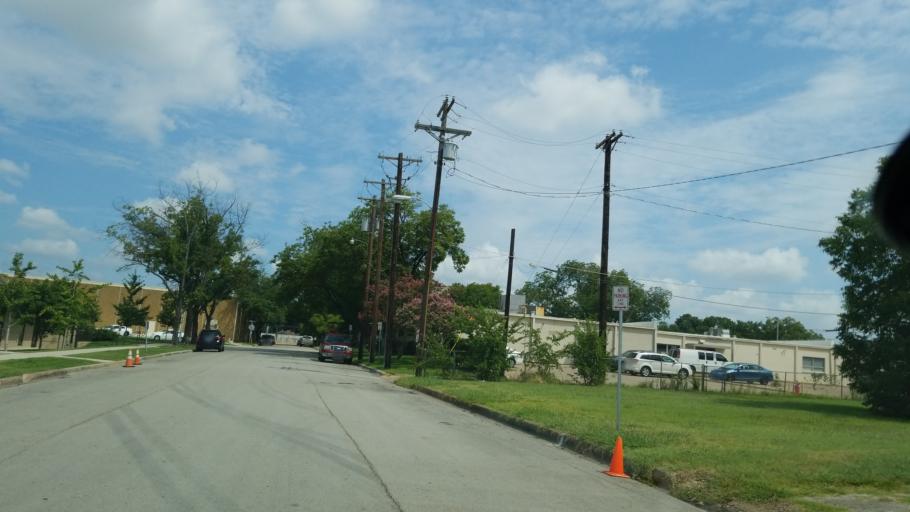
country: US
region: Texas
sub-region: Dallas County
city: Garland
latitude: 32.9119
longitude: -96.6466
